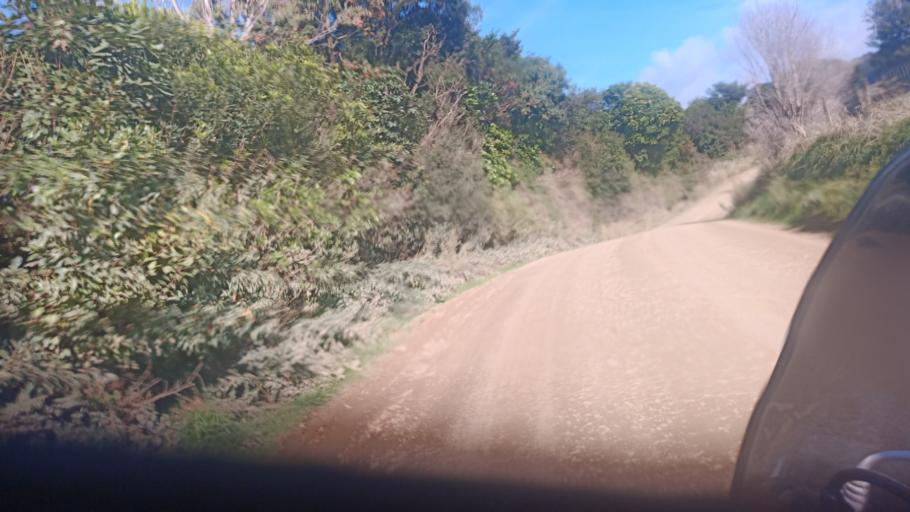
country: NZ
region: Bay of Plenty
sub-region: Opotiki District
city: Opotiki
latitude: -38.4361
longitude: 177.5461
